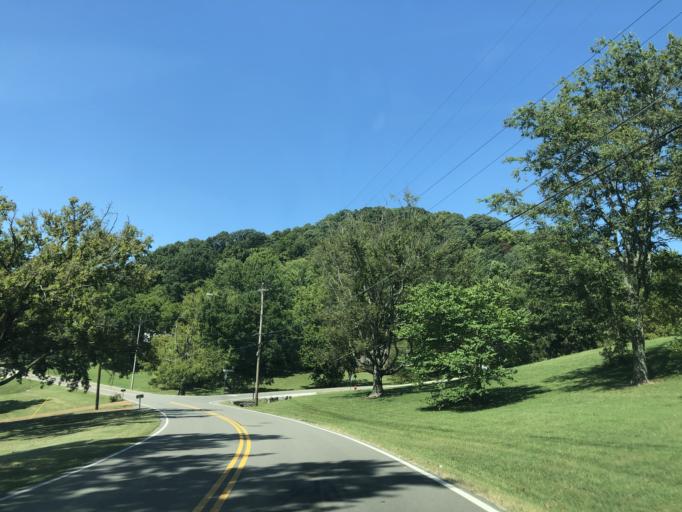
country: US
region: Tennessee
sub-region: Davidson County
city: Forest Hills
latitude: 36.0662
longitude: -86.8310
